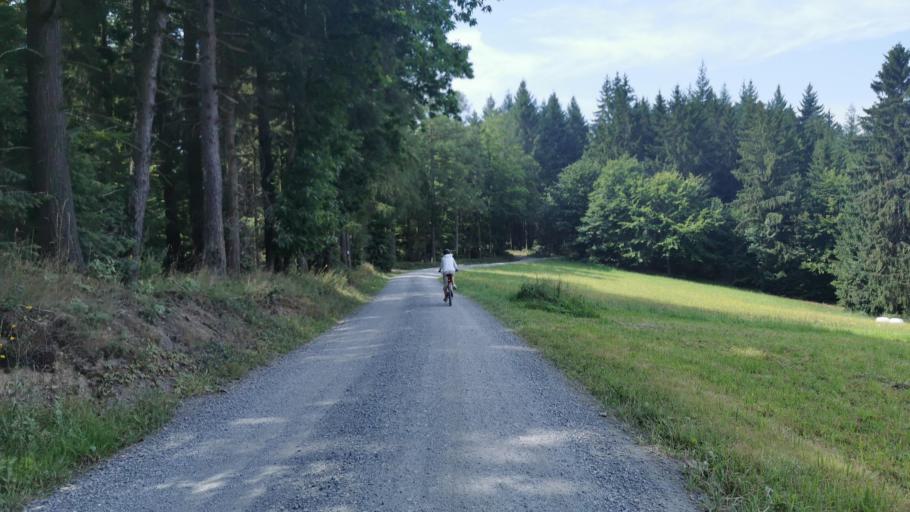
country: DE
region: Bavaria
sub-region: Upper Franconia
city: Wilhelmsthal
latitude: 50.2895
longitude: 11.3982
